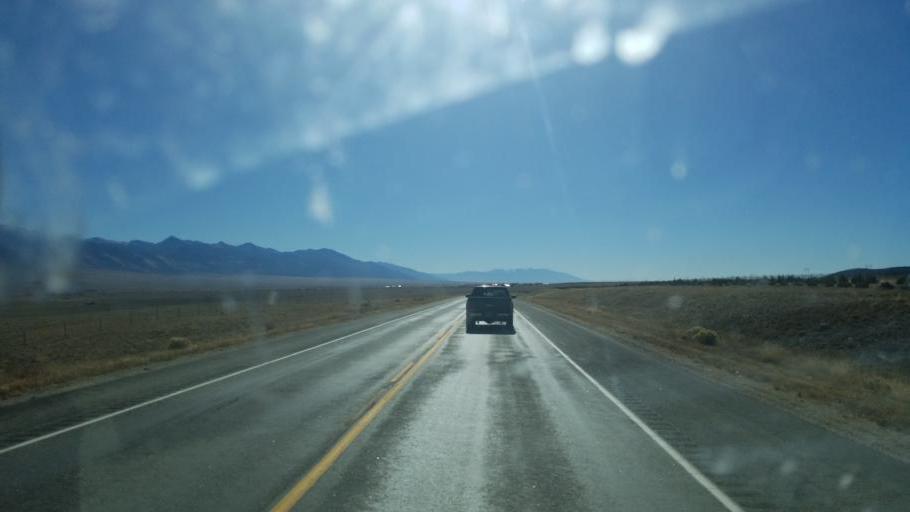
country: US
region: Colorado
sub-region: Saguache County
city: Saguache
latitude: 38.2739
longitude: -105.9687
